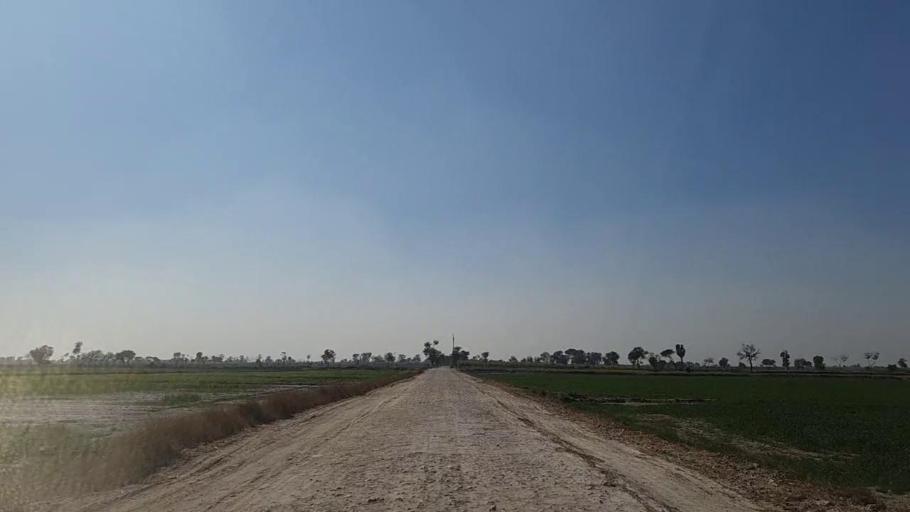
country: PK
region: Sindh
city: Bandhi
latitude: 26.5303
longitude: 68.3014
